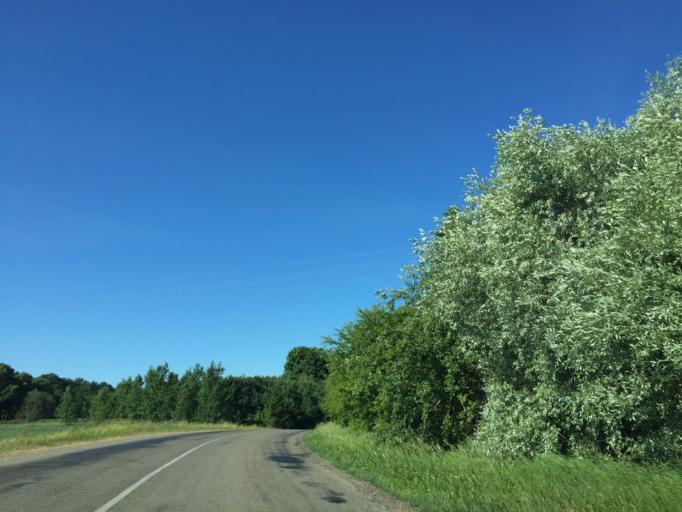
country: LV
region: Aizpute
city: Aizpute
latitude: 56.7207
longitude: 21.6411
